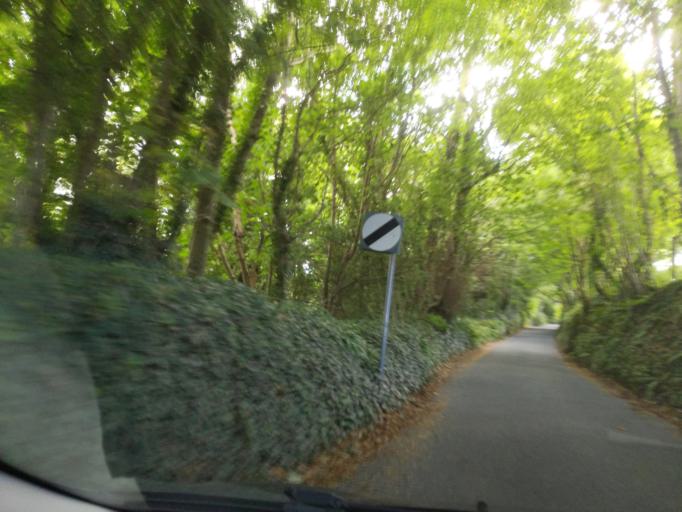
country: GB
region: England
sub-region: Plymouth
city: Plymstock
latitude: 50.3496
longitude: -4.1081
